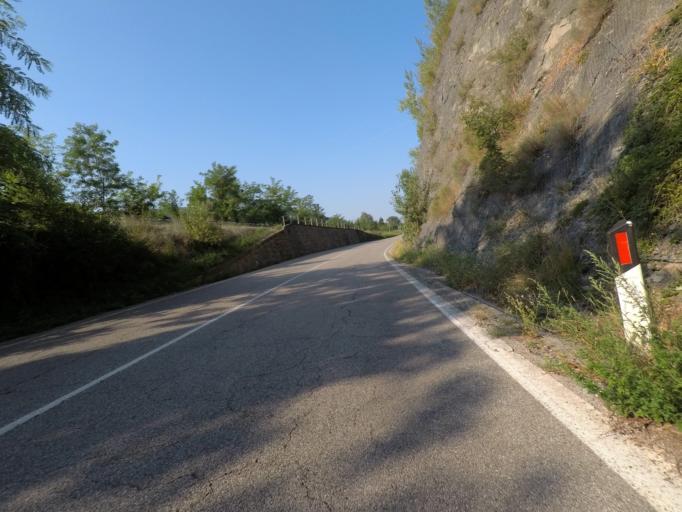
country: IT
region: Friuli Venezia Giulia
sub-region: Provincia di Udine
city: Forgaria nel Friuli
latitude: 46.2178
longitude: 13.0001
